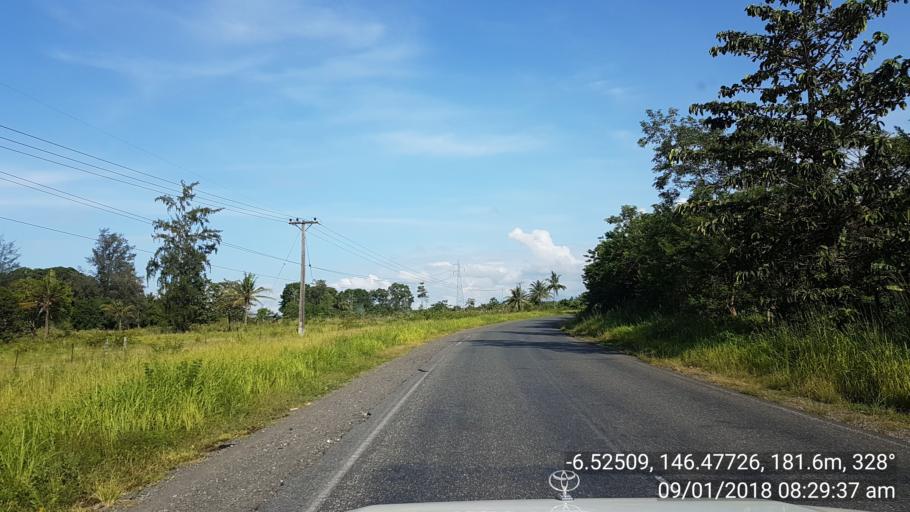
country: PG
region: Morobe
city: Lae
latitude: -6.5250
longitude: 146.4768
